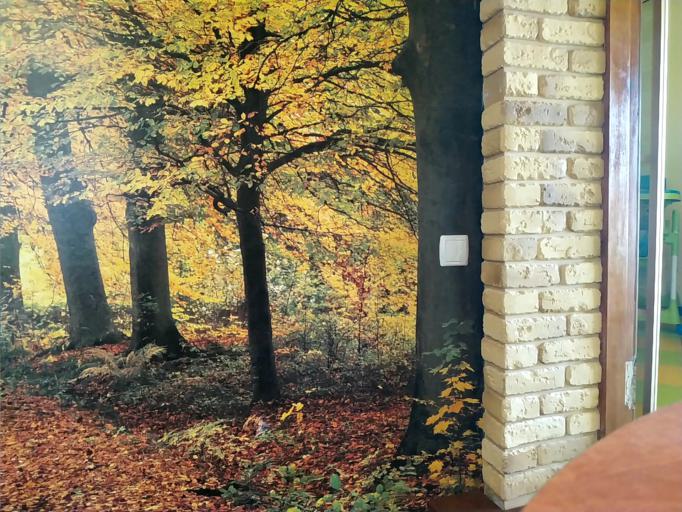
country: RU
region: Tverskaya
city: Rameshki
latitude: 57.5493
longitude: 35.9517
